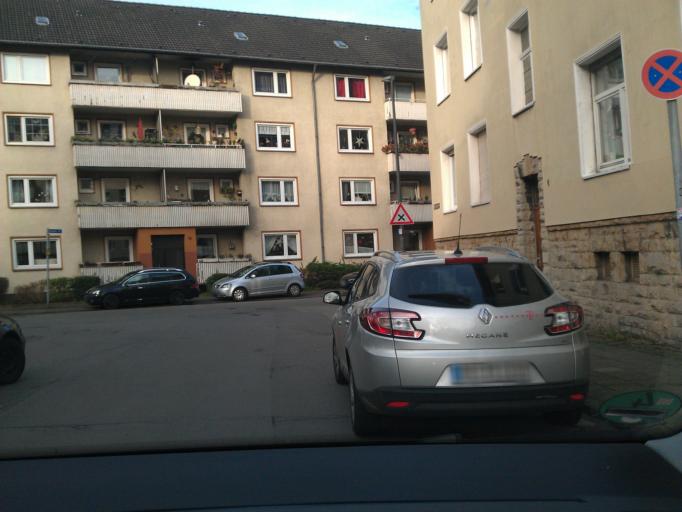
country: DE
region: North Rhine-Westphalia
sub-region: Regierungsbezirk Koln
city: Aachen
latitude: 50.7641
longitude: 6.0839
